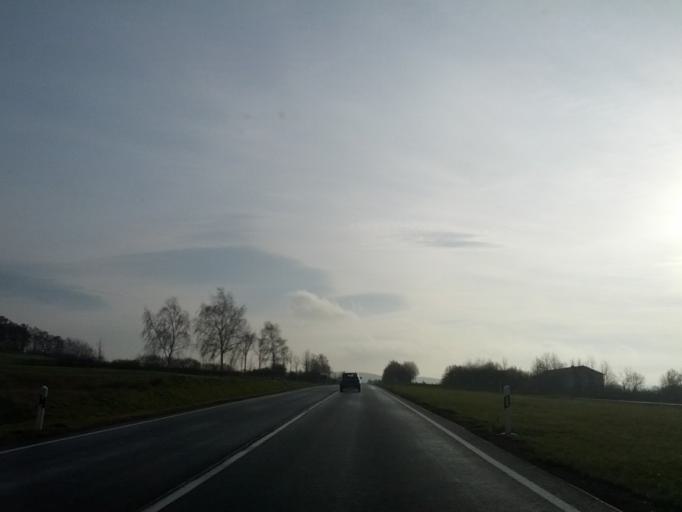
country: DE
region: Thuringia
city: Breitungen
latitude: 50.7705
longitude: 10.3294
